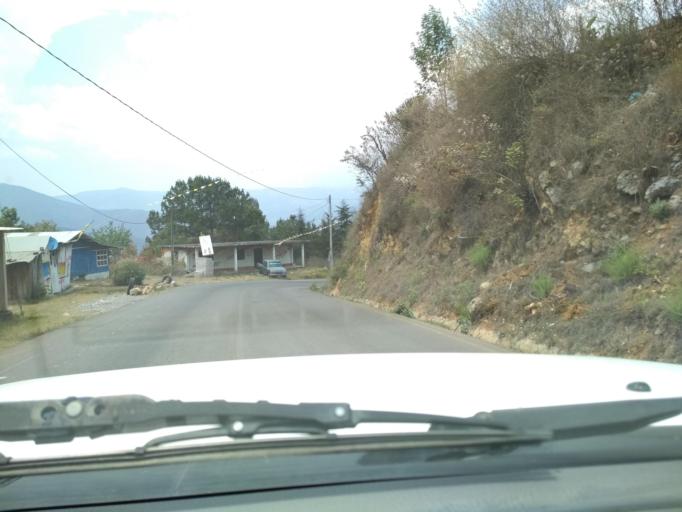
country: MX
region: Veracruz
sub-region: Acultzingo
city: Acatla
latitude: 18.7528
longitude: -97.1967
